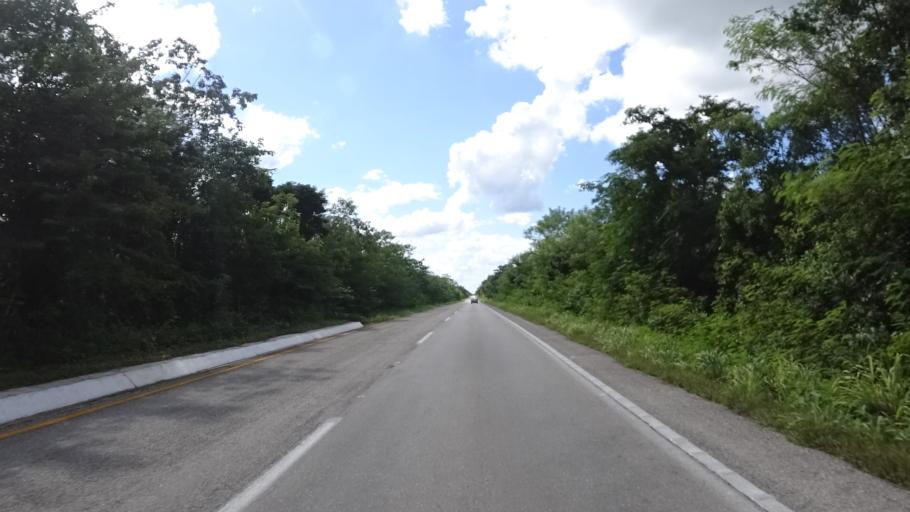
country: MX
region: Yucatan
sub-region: Kantunil
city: Kantunil
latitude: 20.8001
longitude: -88.9991
